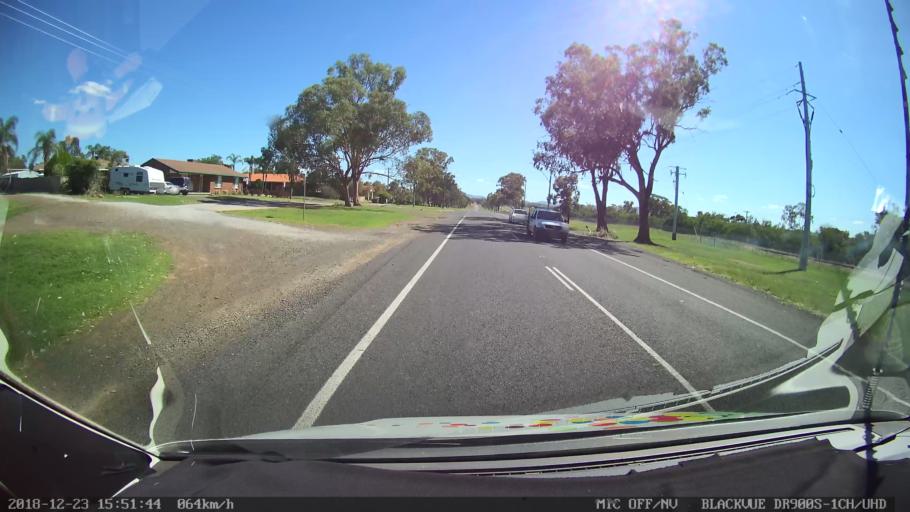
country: AU
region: New South Wales
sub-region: Tamworth Municipality
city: South Tamworth
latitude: -31.1149
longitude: 150.8943
